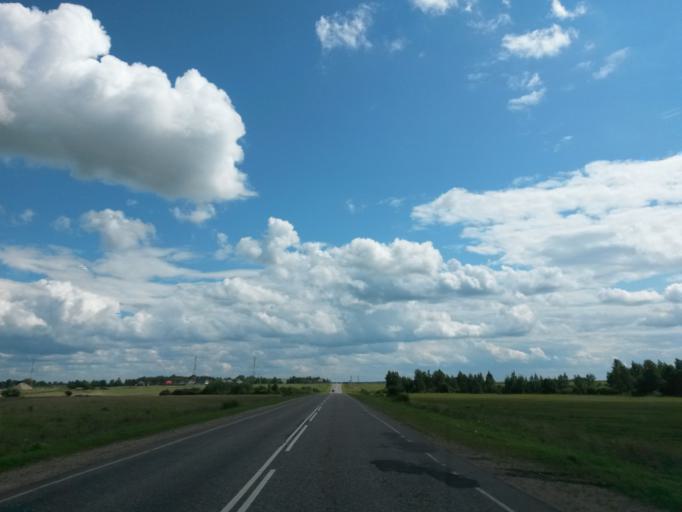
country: RU
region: Ivanovo
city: Pistsovo
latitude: 57.1786
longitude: 40.4915
